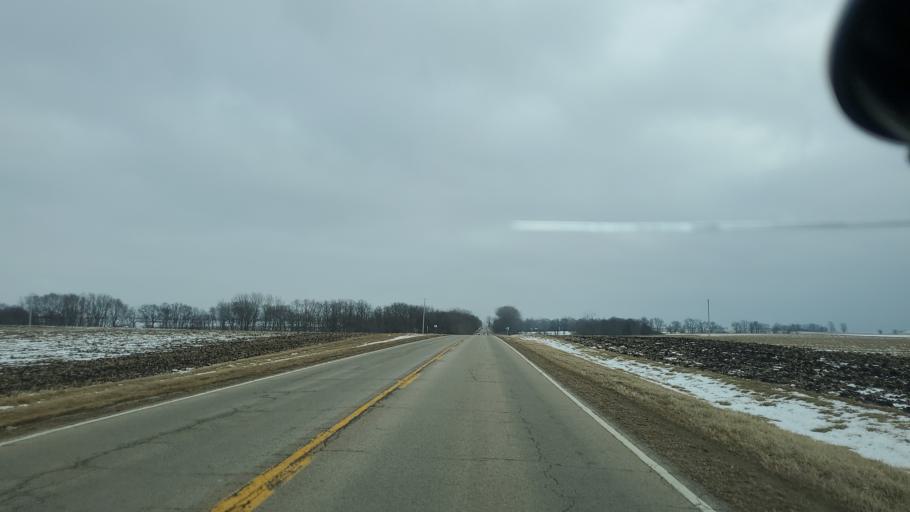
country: US
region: Illinois
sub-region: Marshall County
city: Toluca
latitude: 41.1187
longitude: -89.1649
